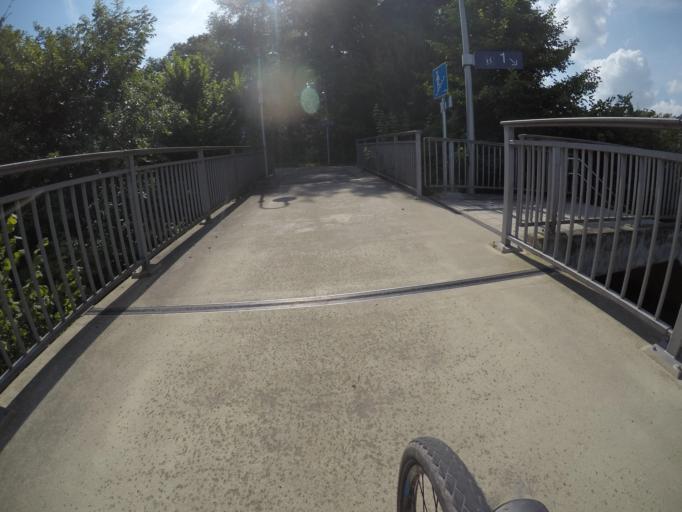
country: DE
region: Baden-Wuerttemberg
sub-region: Karlsruhe Region
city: Olbronn-Durrn
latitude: 48.9932
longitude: 8.7446
